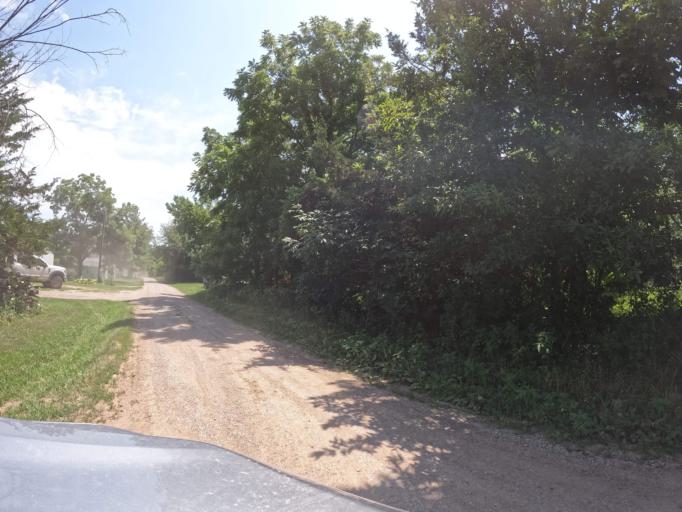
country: US
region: Iowa
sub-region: Appanoose County
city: Centerville
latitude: 40.7736
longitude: -92.9520
